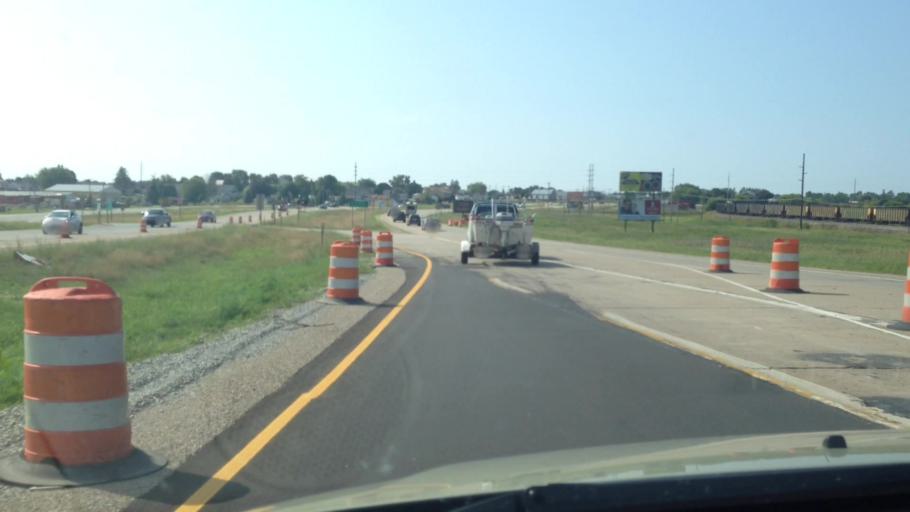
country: US
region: Michigan
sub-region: Delta County
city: Gladstone
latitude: 45.8581
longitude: -87.0248
